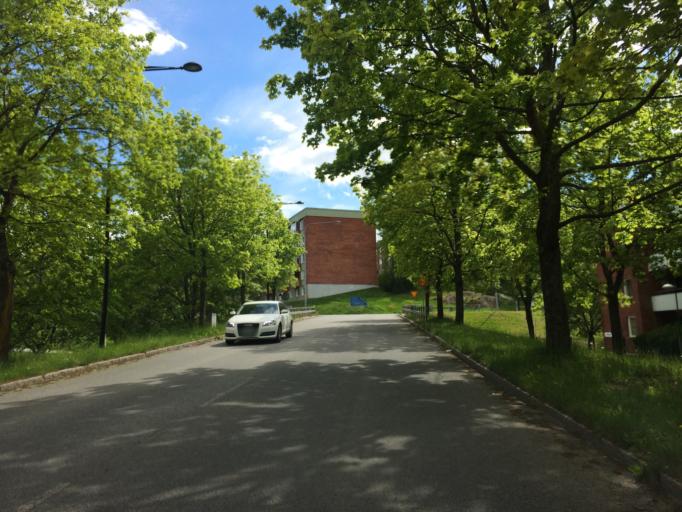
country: SE
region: Stockholm
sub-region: Botkyrka Kommun
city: Fittja
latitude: 59.2641
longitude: 17.8877
